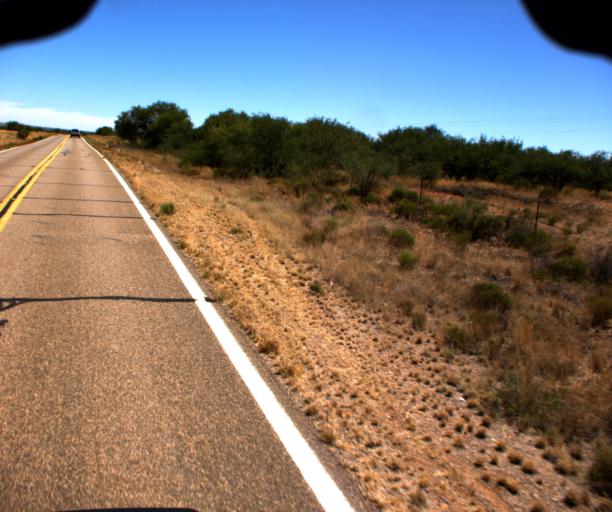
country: US
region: Arizona
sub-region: Pima County
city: Three Points
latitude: 31.6952
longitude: -111.4872
